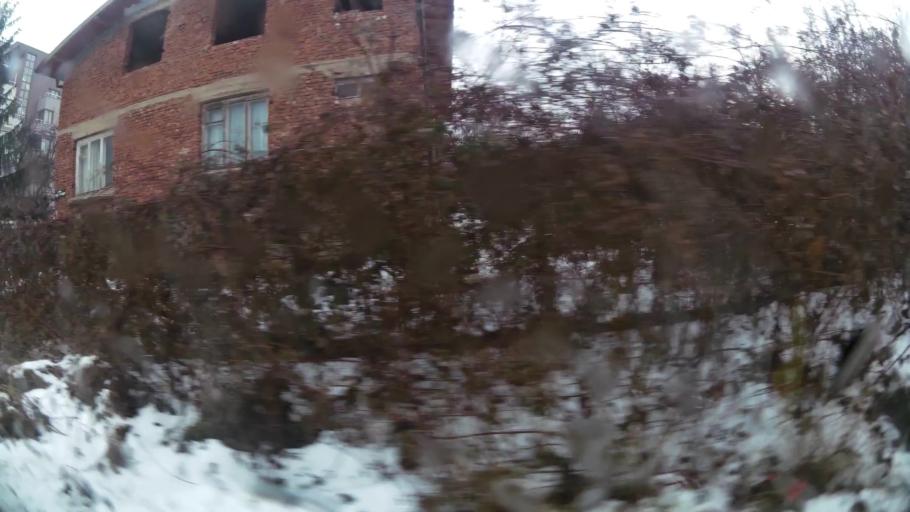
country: BG
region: Sofia-Capital
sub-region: Stolichna Obshtina
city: Sofia
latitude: 42.6759
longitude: 23.2574
